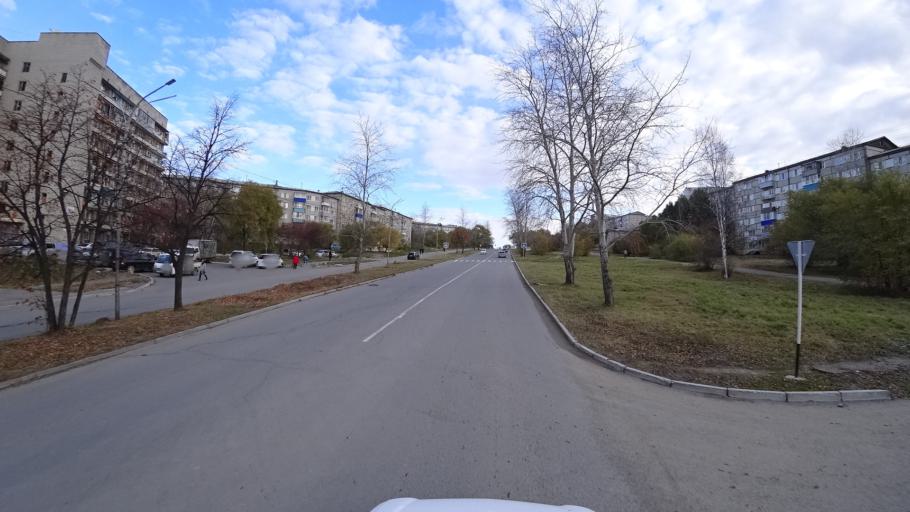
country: RU
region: Khabarovsk Krai
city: Amursk
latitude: 50.2394
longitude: 136.9118
